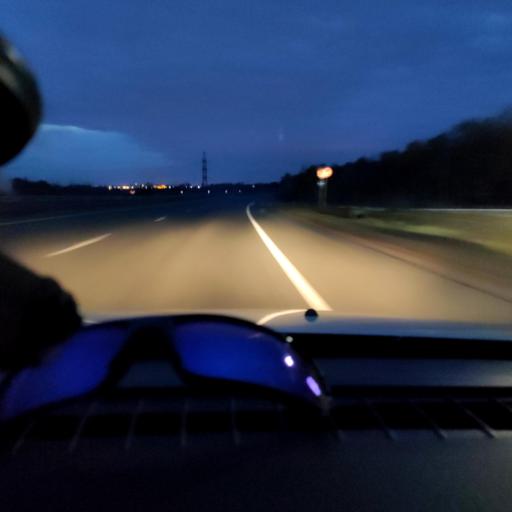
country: RU
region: Samara
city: Novokuybyshevsk
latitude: 53.0234
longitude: 49.9853
